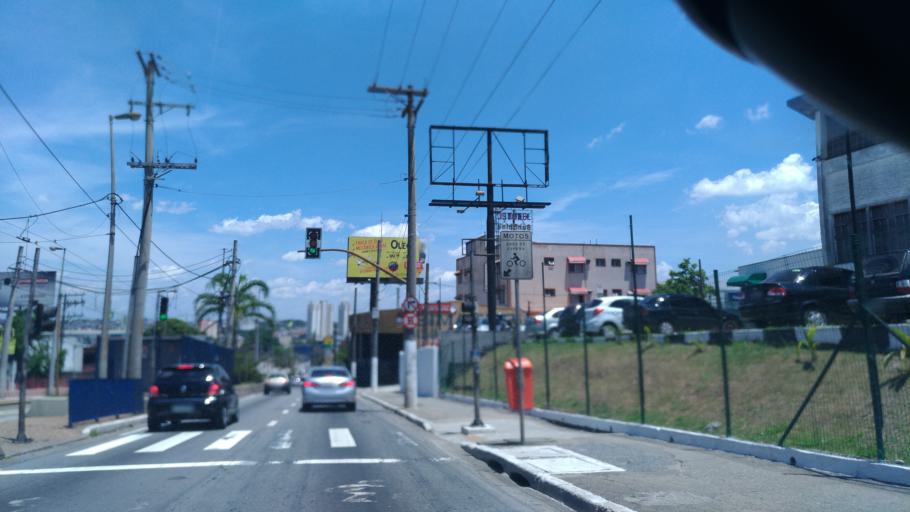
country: BR
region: Sao Paulo
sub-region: Sao Bernardo Do Campo
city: Sao Bernardo do Campo
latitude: -23.6897
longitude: -46.5687
